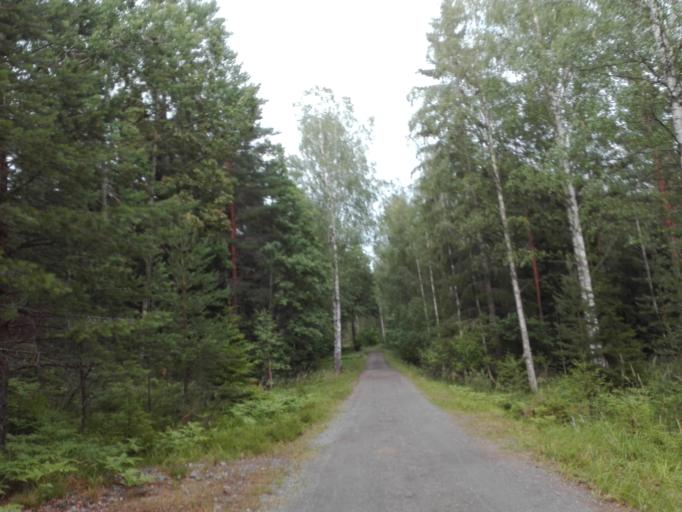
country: SE
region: Stockholm
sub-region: Nacka Kommun
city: Fisksatra
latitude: 59.2819
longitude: 18.2287
